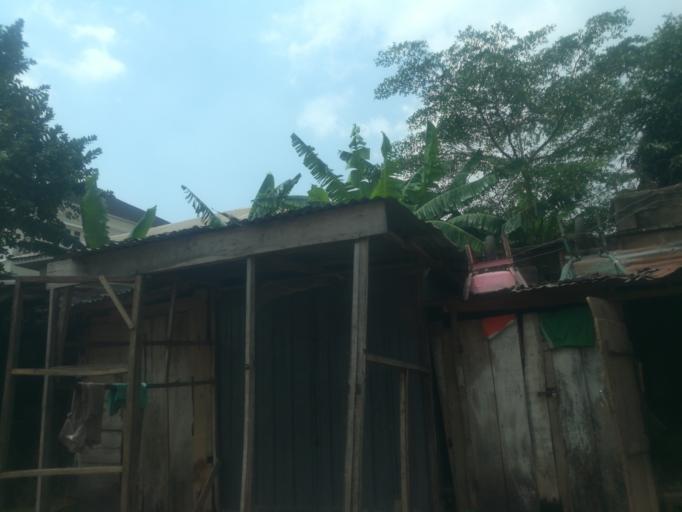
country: NG
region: Oyo
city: Ibadan
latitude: 7.3953
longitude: 3.9528
